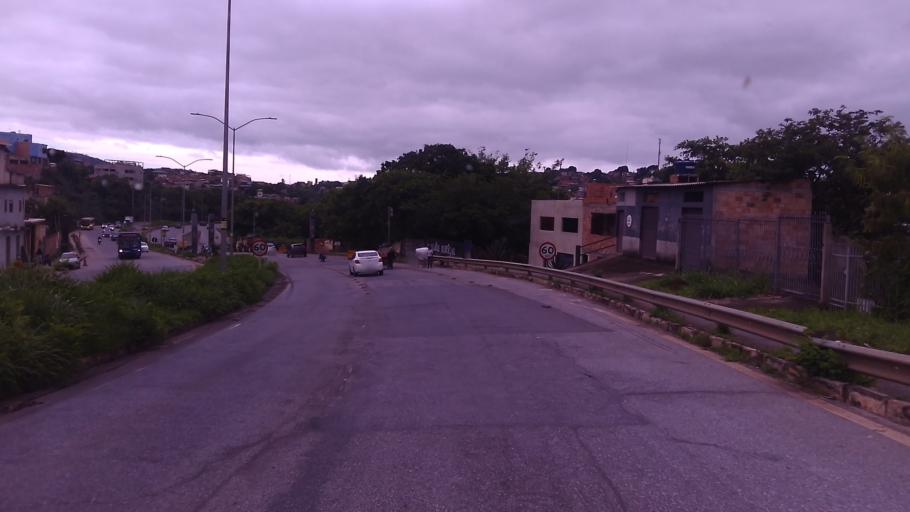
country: BR
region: Minas Gerais
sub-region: Santa Luzia
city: Santa Luzia
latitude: -19.8369
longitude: -43.9078
